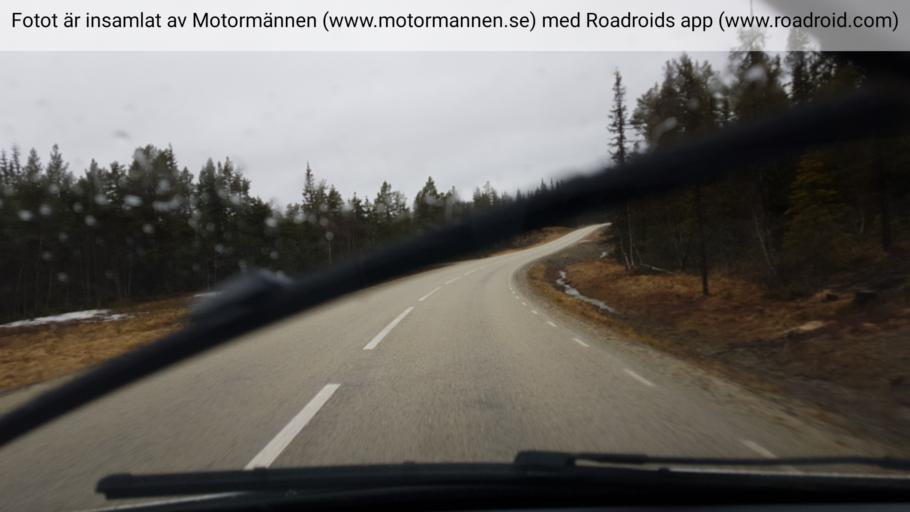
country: SE
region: Jaemtland
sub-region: Are Kommun
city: Are
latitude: 62.8408
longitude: 12.8300
